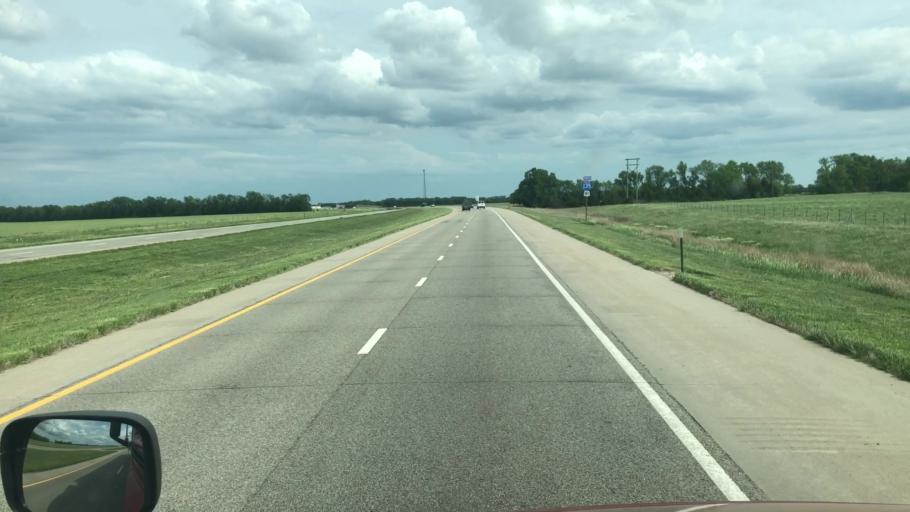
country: US
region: Kansas
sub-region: McPherson County
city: Moundridge
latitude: 38.1987
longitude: -97.4833
